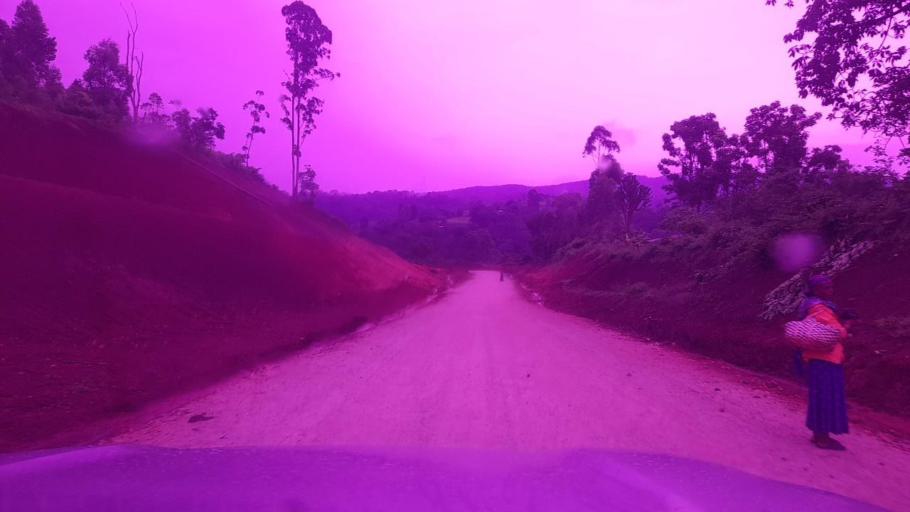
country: ET
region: Southern Nations, Nationalities, and People's Region
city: Bonga
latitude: 7.4520
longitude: 36.1373
